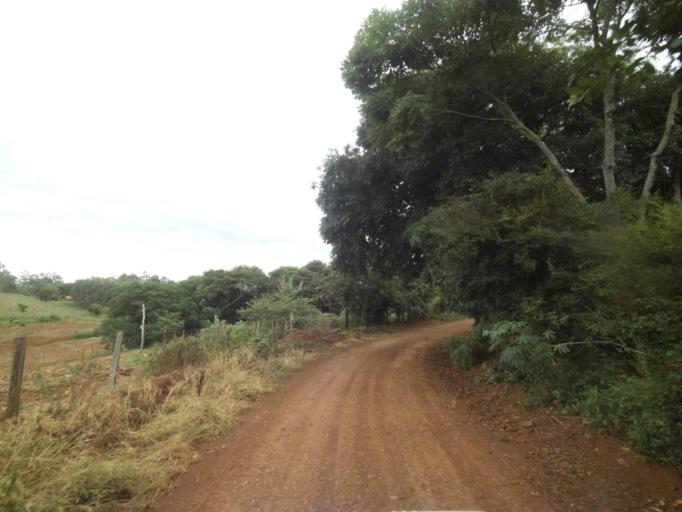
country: BR
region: Parana
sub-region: Guaraniacu
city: Guaraniacu
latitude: -24.9127
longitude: -52.9367
